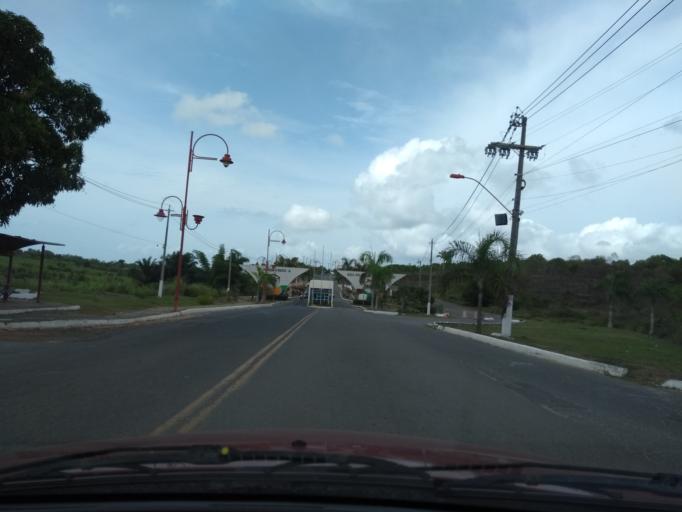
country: BR
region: Bahia
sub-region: Sao Francisco Do Conde
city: Sao Francisco do Conde
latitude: -12.6125
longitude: -38.6548
